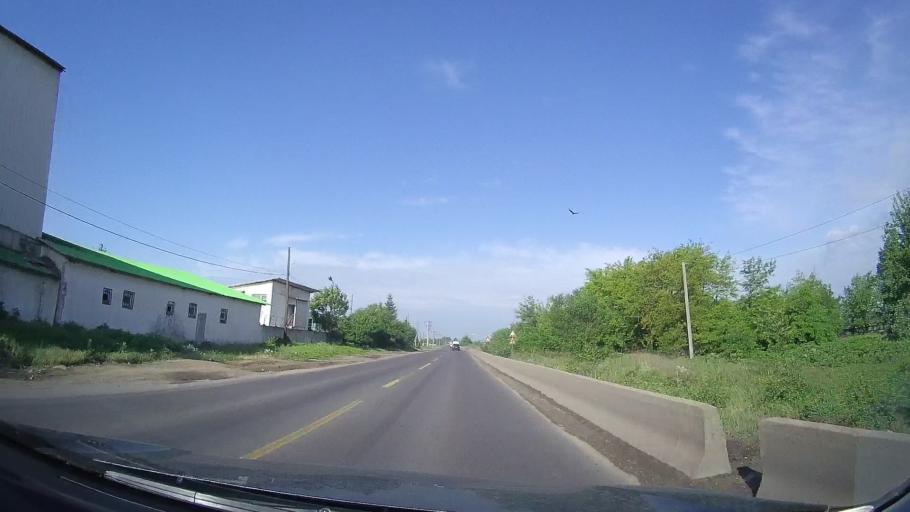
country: RO
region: Ilfov
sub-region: Comuna Berceni
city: Berceni
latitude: 44.3376
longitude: 26.1483
